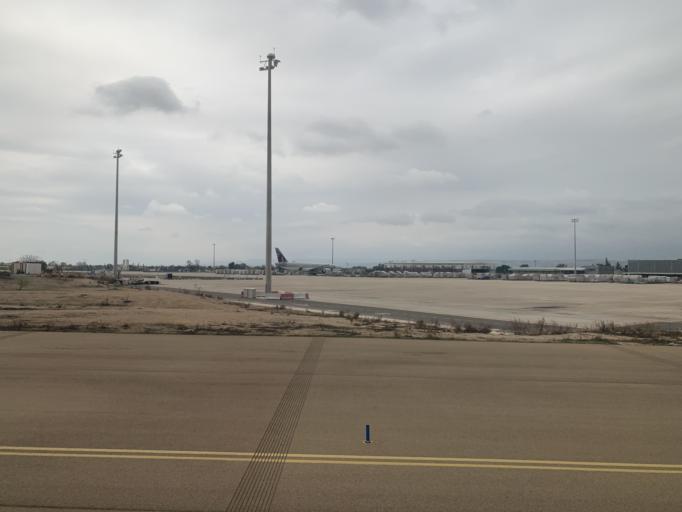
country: ES
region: Aragon
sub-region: Provincia de Zaragoza
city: Utebo
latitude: 41.6620
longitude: -1.0119
